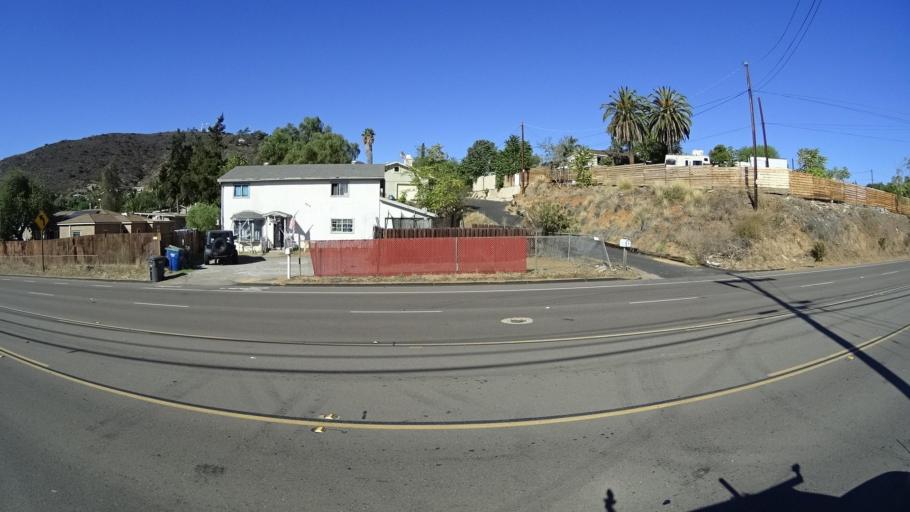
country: US
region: California
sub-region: San Diego County
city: Winter Gardens
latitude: 32.8297
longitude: -116.9328
